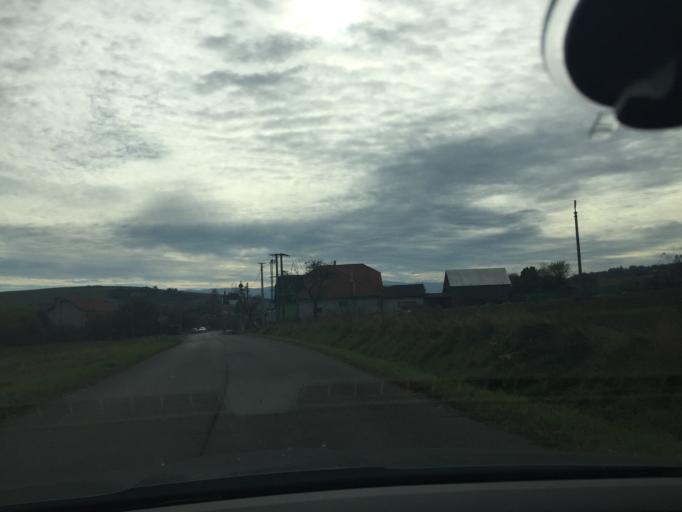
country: SK
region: Presovsky
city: Spisske Podhradie
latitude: 48.9850
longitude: 20.7939
